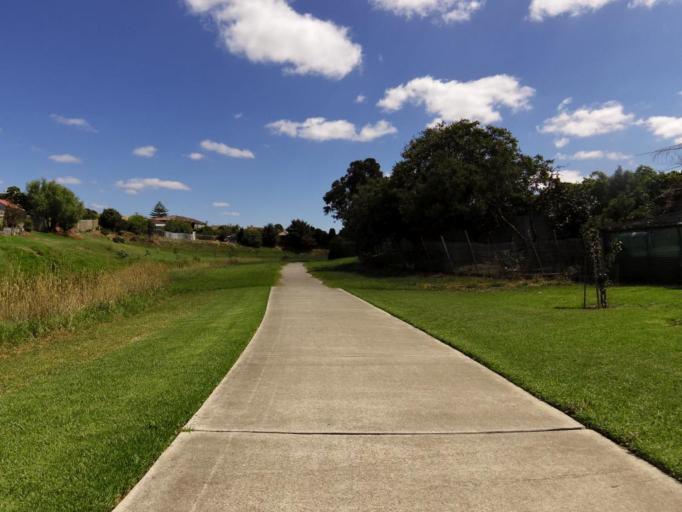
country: AU
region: Victoria
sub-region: Whittlesea
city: Thomastown
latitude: -37.6836
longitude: 145.0080
